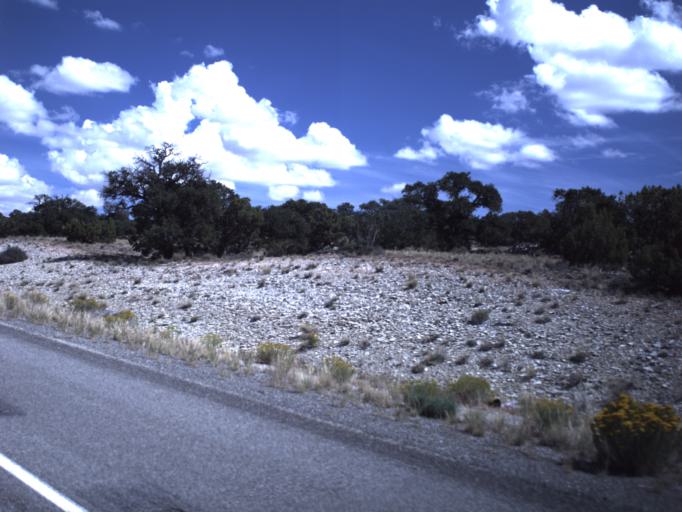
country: US
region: Utah
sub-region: Emery County
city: Ferron
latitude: 38.8429
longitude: -110.9504
